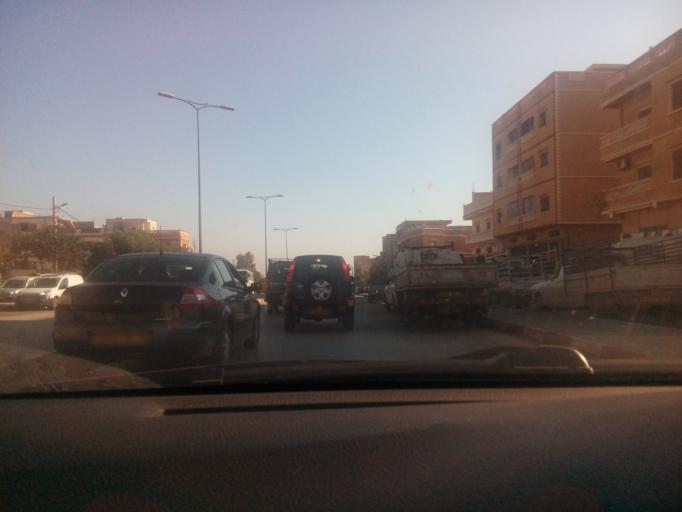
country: DZ
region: Oran
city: Oran
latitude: 35.6611
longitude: -0.6902
